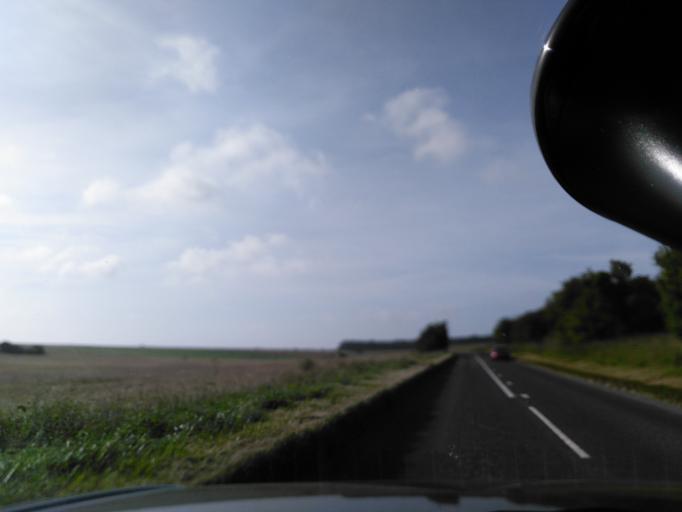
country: GB
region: England
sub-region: Wiltshire
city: Market Lavington
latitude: 51.2374
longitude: -1.9726
